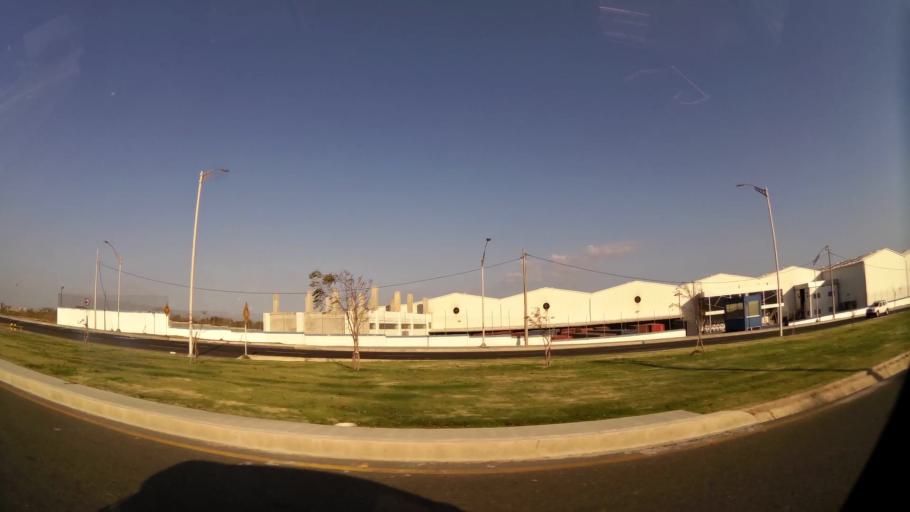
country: CO
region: Atlantico
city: Barranquilla
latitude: 11.0342
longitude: -74.8300
